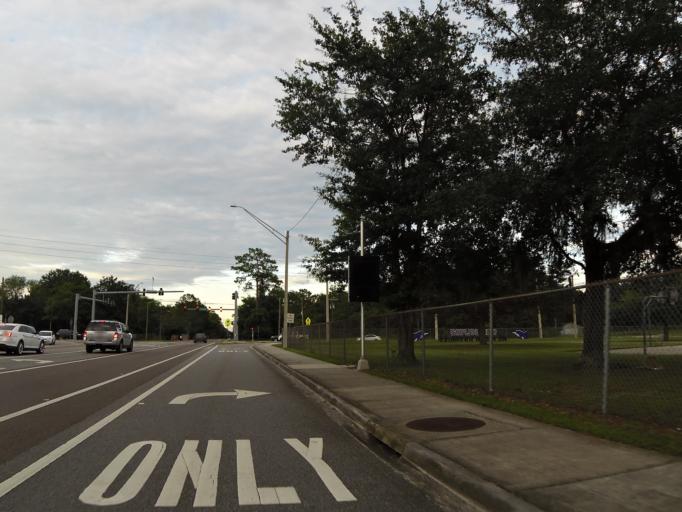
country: US
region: Florida
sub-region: Clay County
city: Bellair-Meadowbrook Terrace
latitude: 30.3022
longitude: -81.7989
